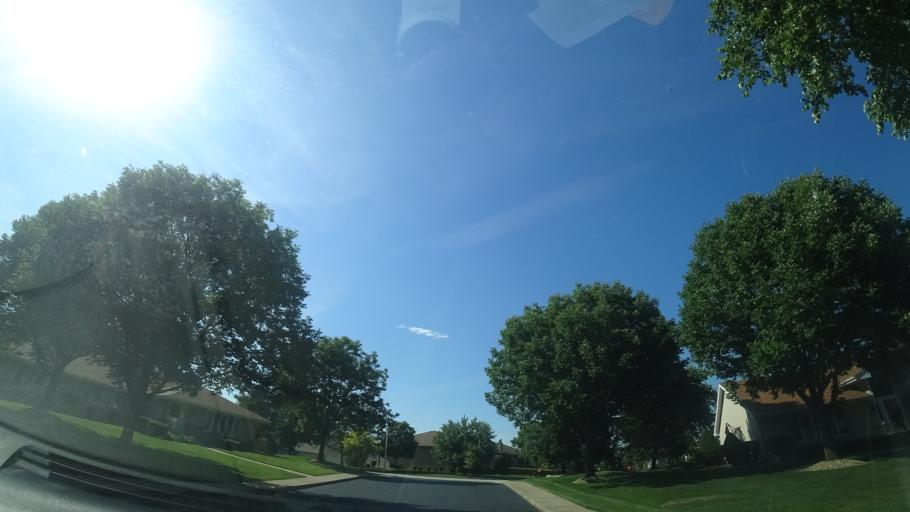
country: US
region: Illinois
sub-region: Will County
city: Mokena
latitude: 41.5653
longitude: -87.8822
